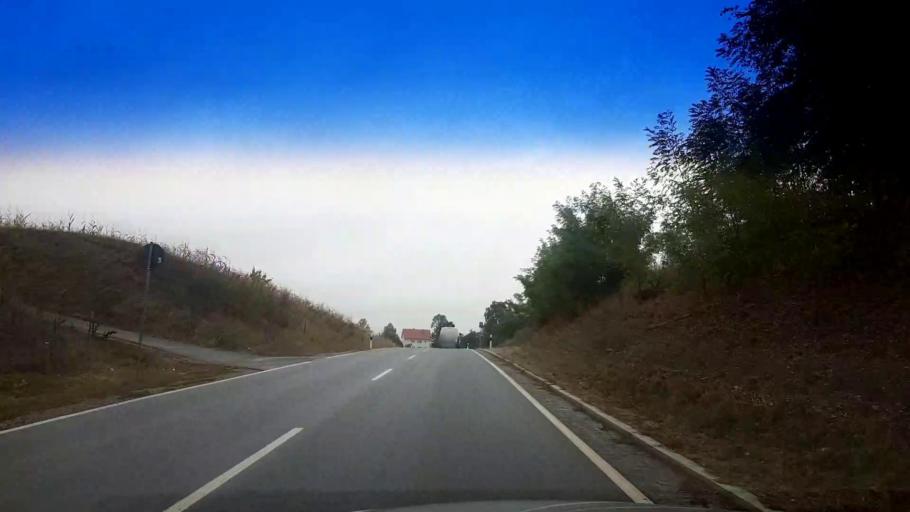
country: DE
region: Bavaria
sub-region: Upper Franconia
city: Buttenheim
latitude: 49.7988
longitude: 11.0340
